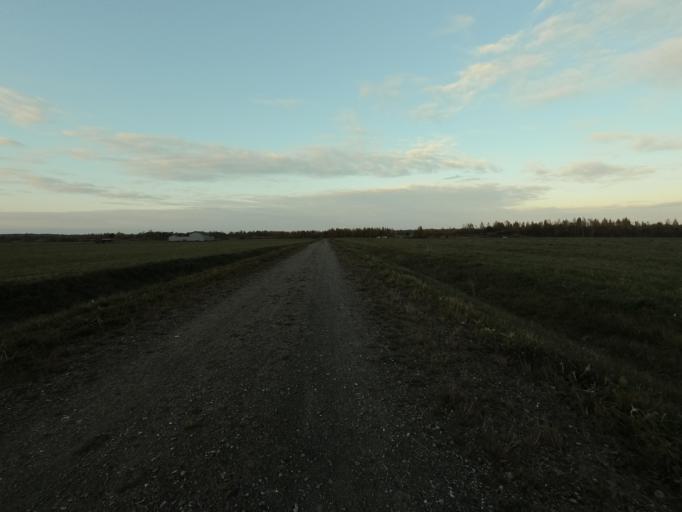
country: RU
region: Leningrad
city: Mga
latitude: 59.7874
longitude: 31.1991
